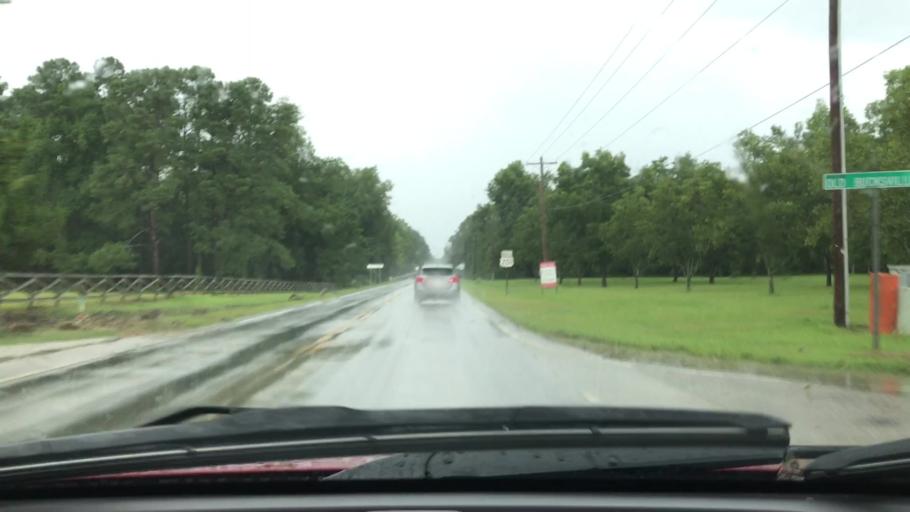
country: US
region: South Carolina
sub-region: Horry County
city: Conway
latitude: 33.7482
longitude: -79.0784
